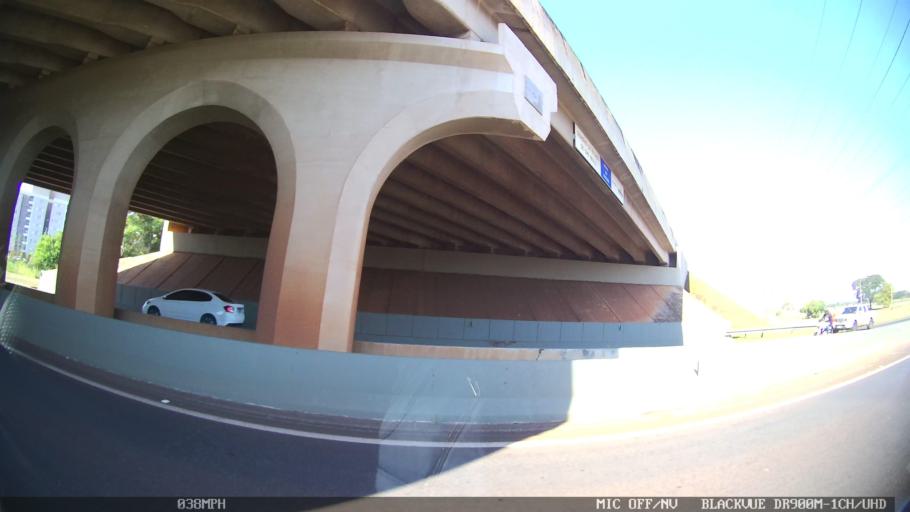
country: BR
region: Sao Paulo
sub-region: Ribeirao Preto
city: Ribeirao Preto
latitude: -21.2152
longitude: -47.7732
